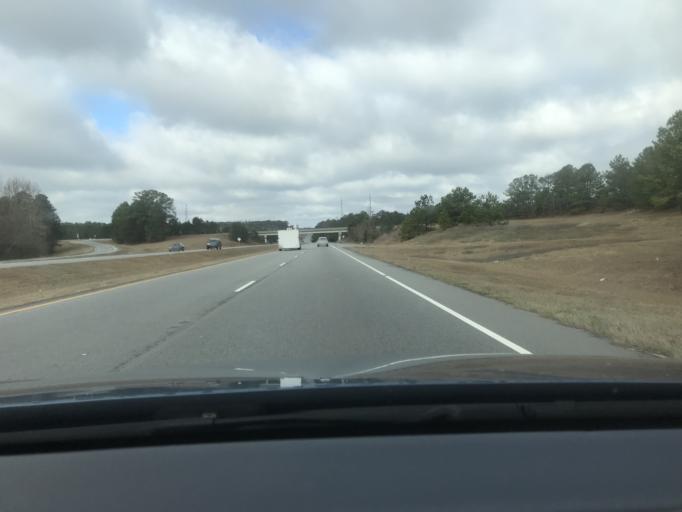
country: US
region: North Carolina
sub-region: Cumberland County
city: Spring Lake
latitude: 35.2682
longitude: -79.0573
